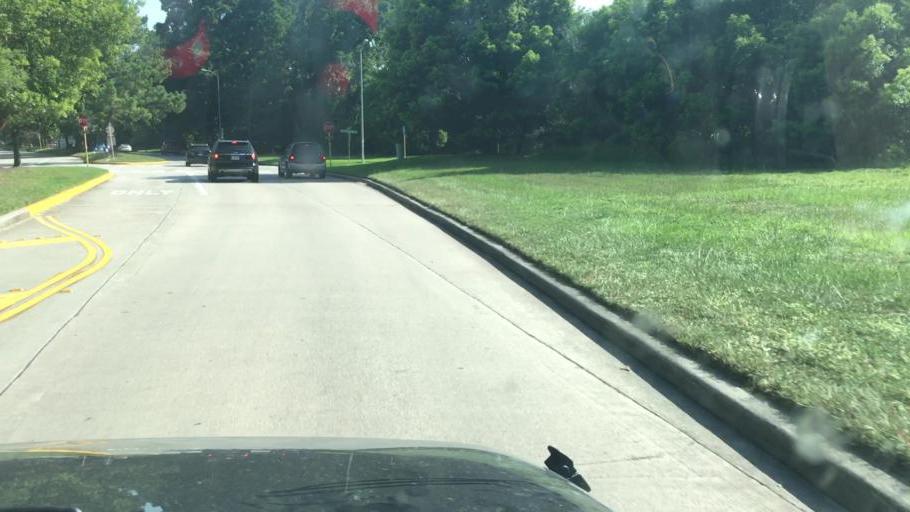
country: US
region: Texas
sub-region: Harris County
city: Atascocita
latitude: 30.0013
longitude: -95.1781
